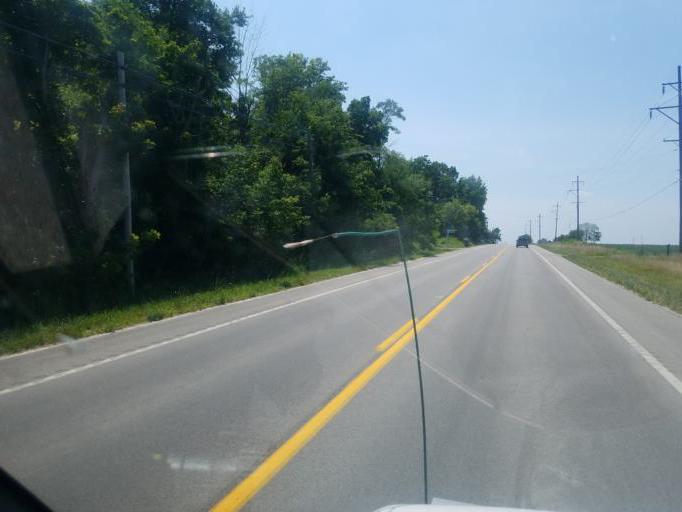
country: US
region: Ohio
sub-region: Mercer County
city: Celina
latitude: 40.5511
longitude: -84.4879
